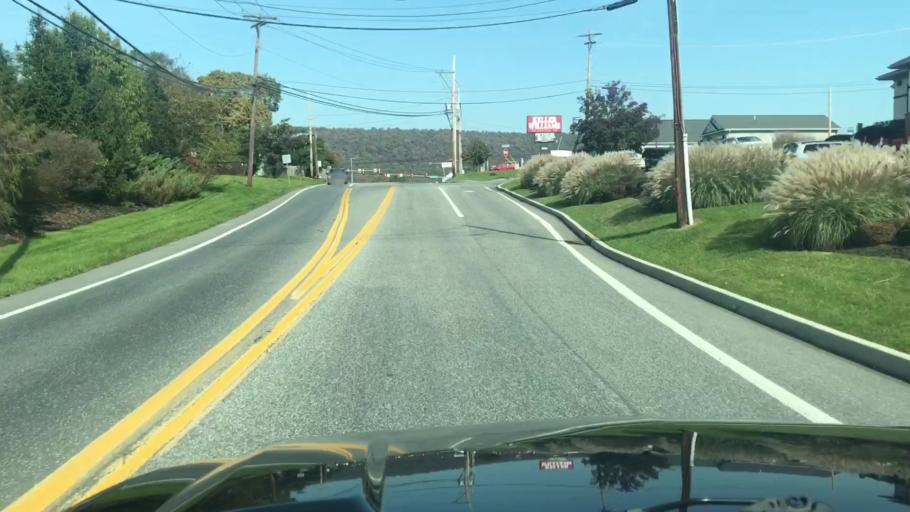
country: US
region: Pennsylvania
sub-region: Cumberland County
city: Enola
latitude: 40.2874
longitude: -76.9866
